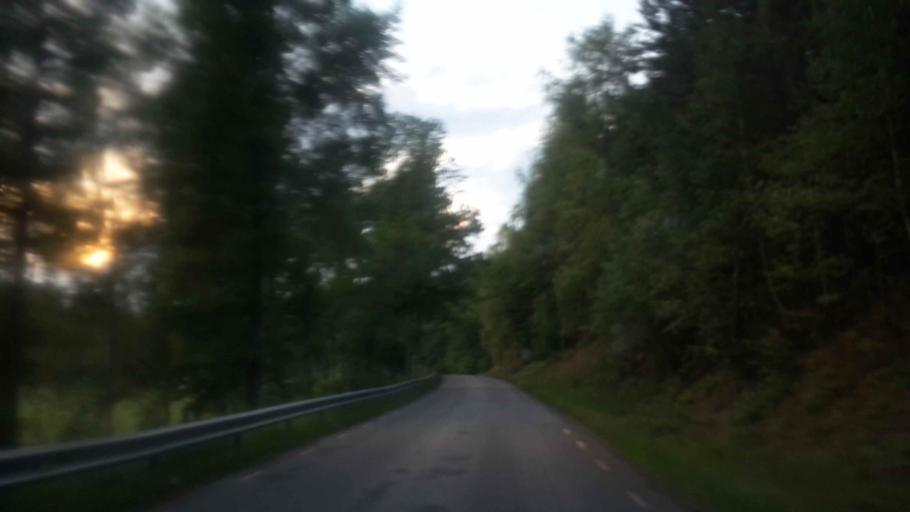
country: SE
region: OEstergoetland
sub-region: Atvidabergs Kommun
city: Atvidaberg
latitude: 58.2796
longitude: 16.1546
